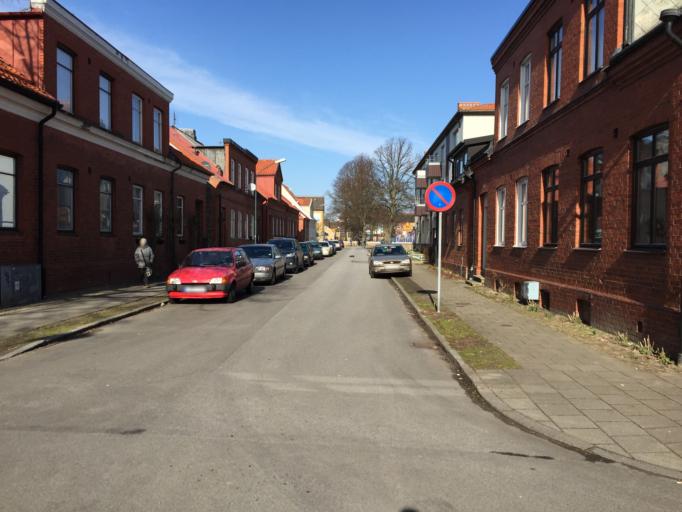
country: SE
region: Skane
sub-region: Trelleborgs Kommun
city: Trelleborg
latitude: 55.3773
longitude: 13.1619
